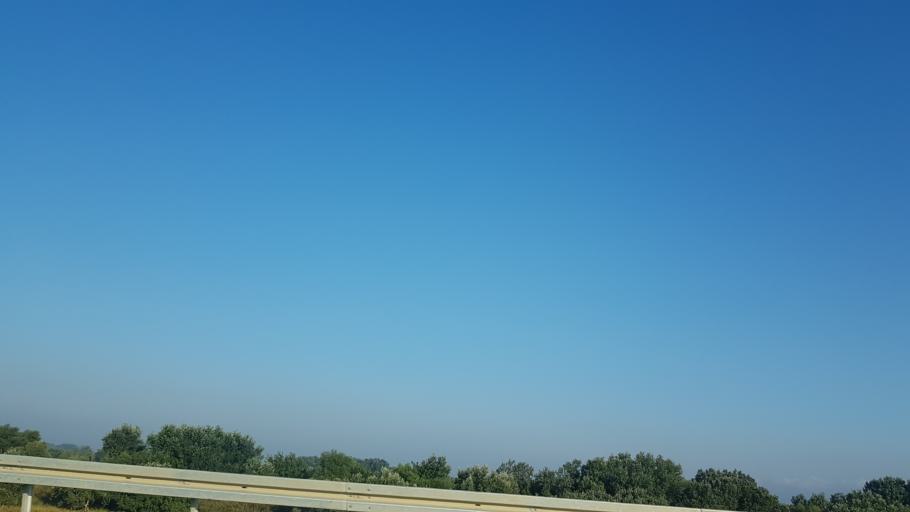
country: TR
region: Bursa
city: Karacabey
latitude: 40.1800
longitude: 28.3291
